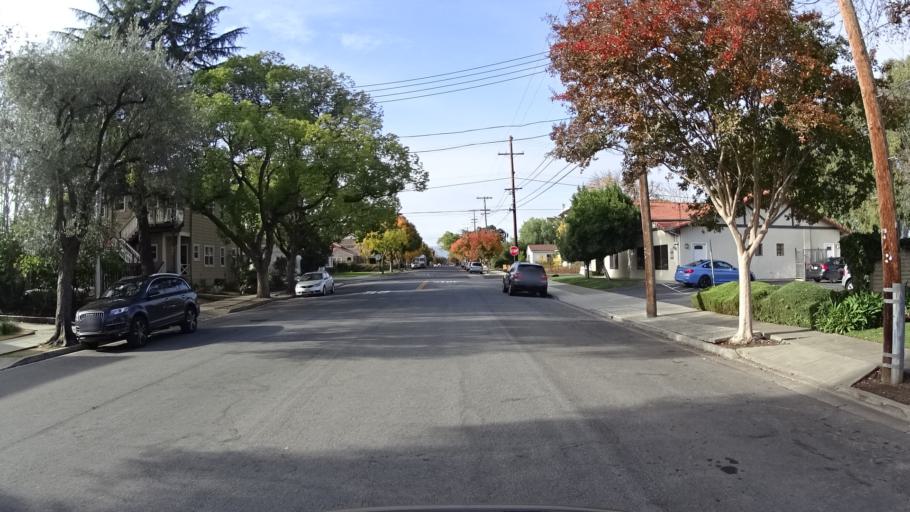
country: US
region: California
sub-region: Santa Clara County
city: Santa Clara
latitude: 37.3523
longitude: -121.9438
